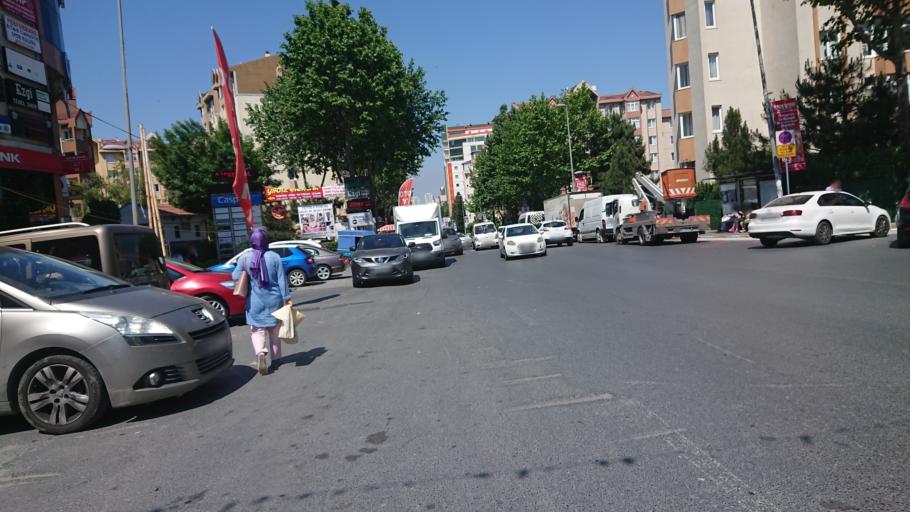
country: TR
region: Istanbul
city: Esenyurt
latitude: 41.0607
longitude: 28.6766
